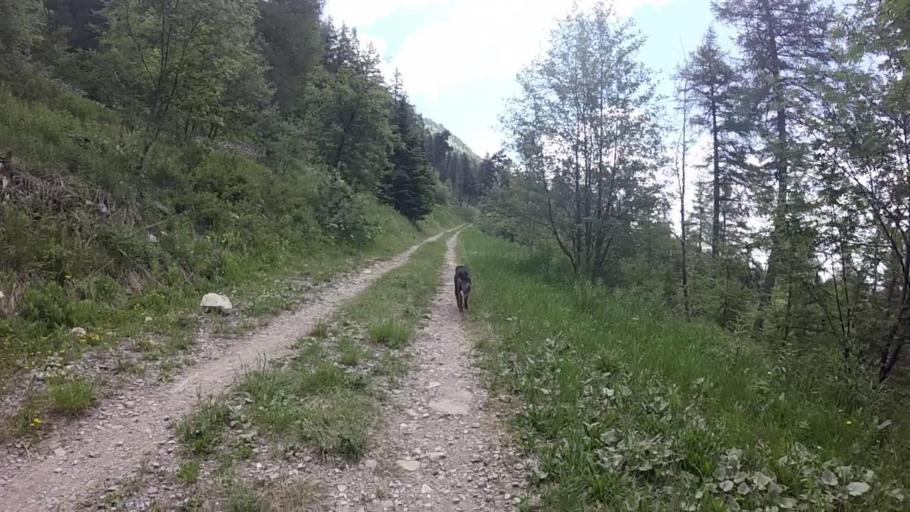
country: FR
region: Provence-Alpes-Cote d'Azur
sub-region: Departement des Alpes-de-Haute-Provence
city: Seyne-les-Alpes
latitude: 44.4016
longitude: 6.3785
